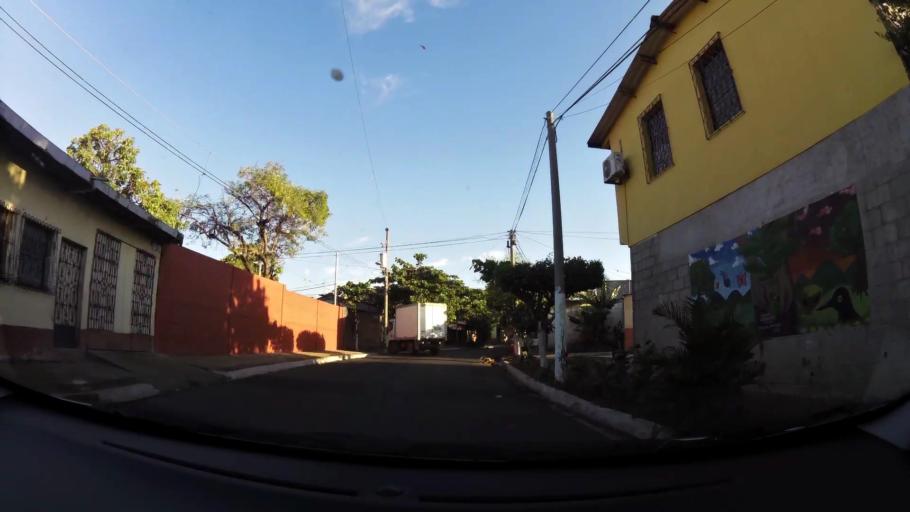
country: SV
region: Sonsonate
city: San Antonio del Monte
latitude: 13.7073
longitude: -89.7340
